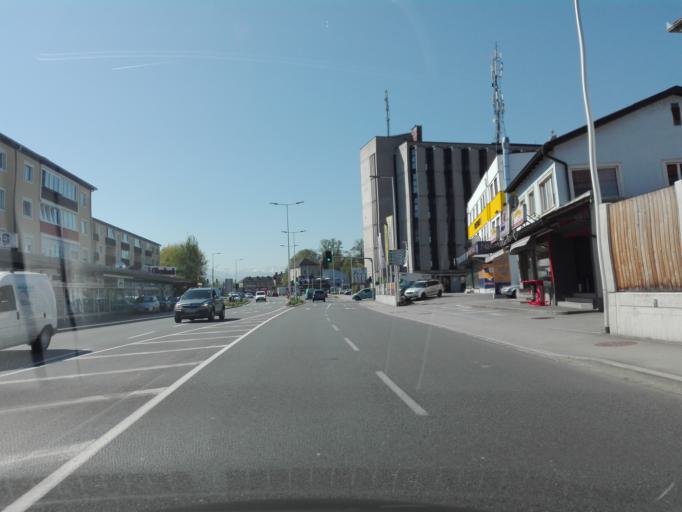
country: AT
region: Upper Austria
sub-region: Steyr Stadt
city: Steyr
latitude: 48.0518
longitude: 14.4203
